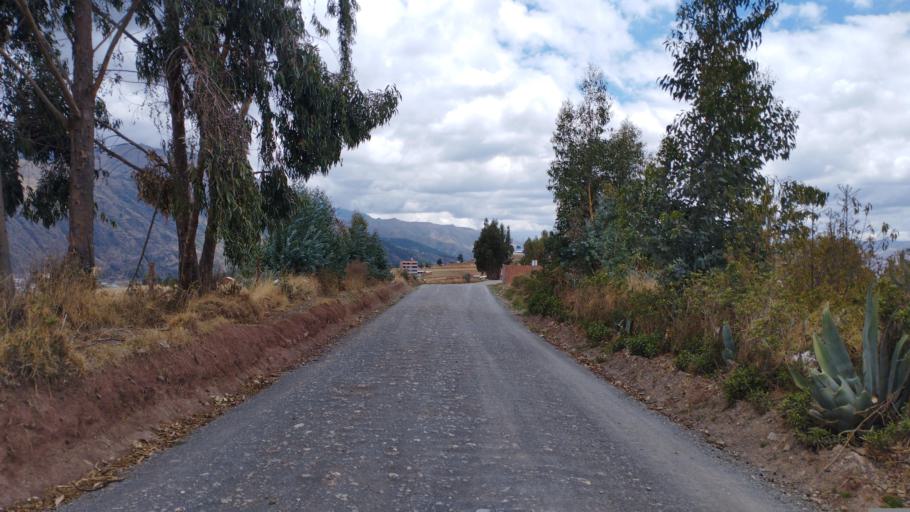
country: PE
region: Cusco
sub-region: Provincia de Cusco
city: Cusco
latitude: -13.5118
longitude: -71.9394
